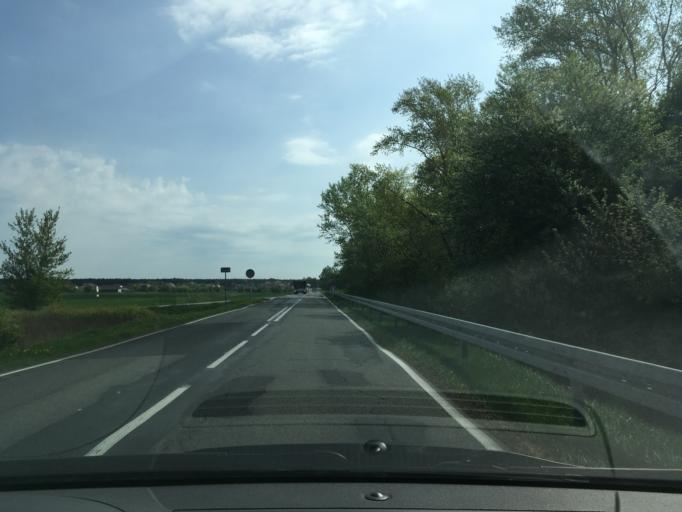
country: PL
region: Lublin Voivodeship
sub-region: Powiat pulawski
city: Pulawy
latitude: 51.4757
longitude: 21.8963
